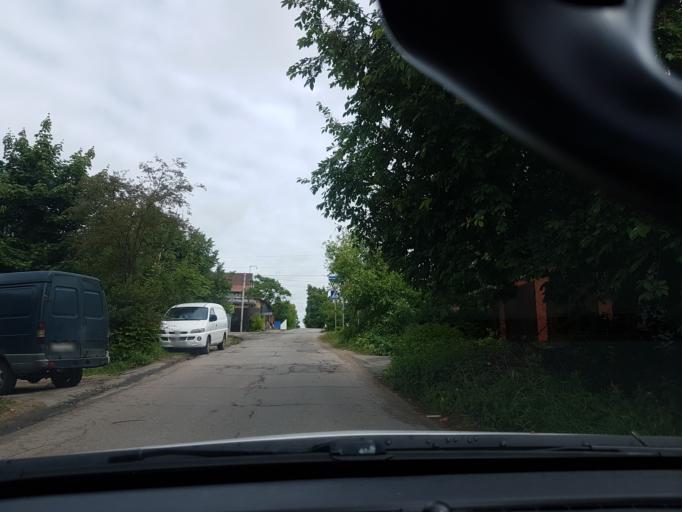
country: RU
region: Moskovskaya
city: Istra
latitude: 55.9236
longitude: 36.8620
